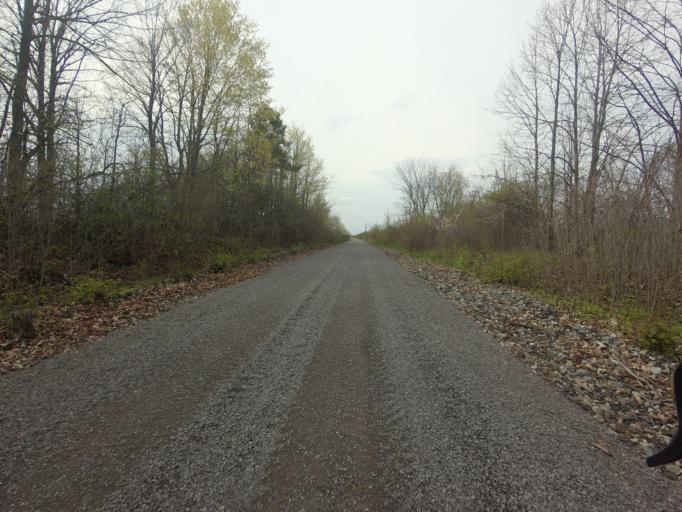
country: CA
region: Ontario
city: Carleton Place
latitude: 45.1996
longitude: -76.1669
